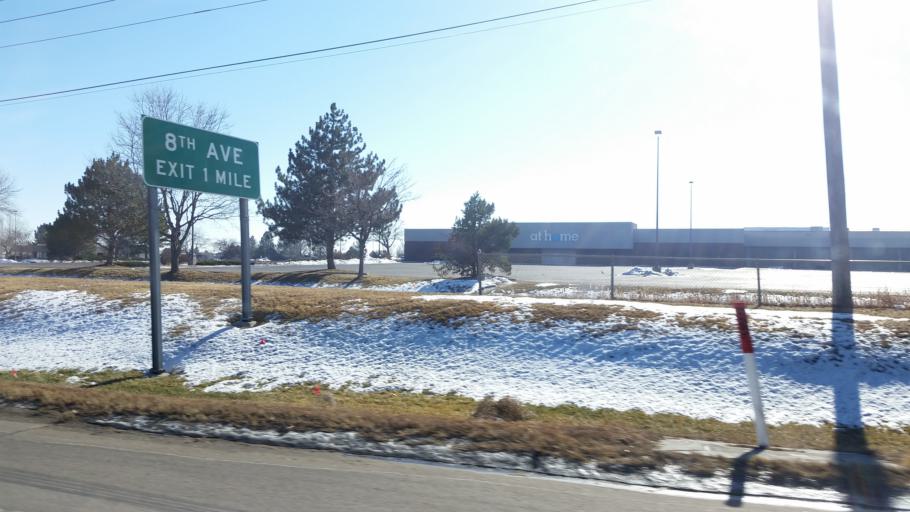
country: US
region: Colorado
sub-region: Weld County
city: Evans
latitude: 40.3920
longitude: -104.7106
